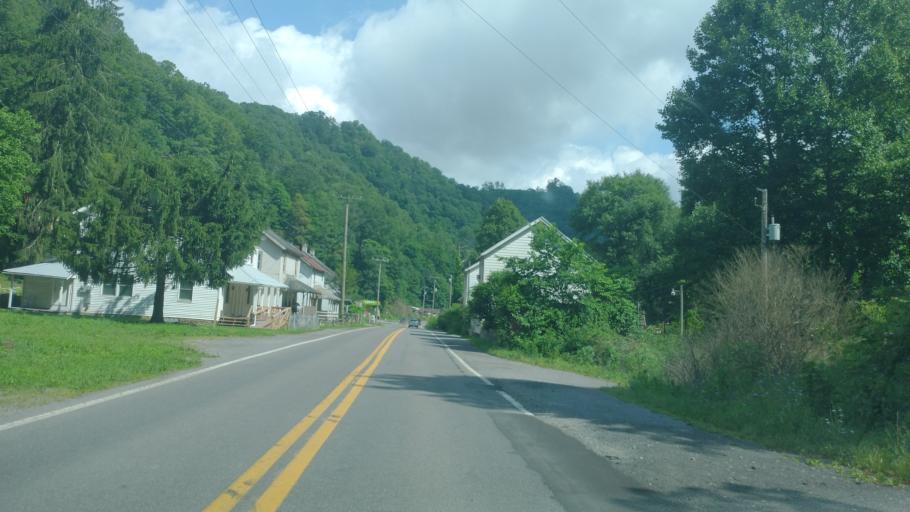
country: US
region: West Virginia
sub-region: McDowell County
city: Welch
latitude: 37.3926
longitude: -81.4212
